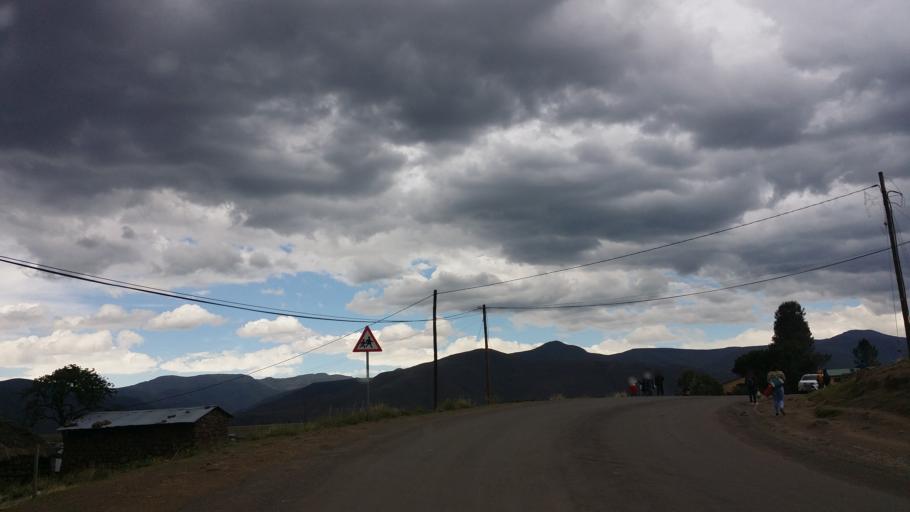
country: LS
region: Mokhotlong
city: Mokhotlong
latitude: -29.2889
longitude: 29.0613
